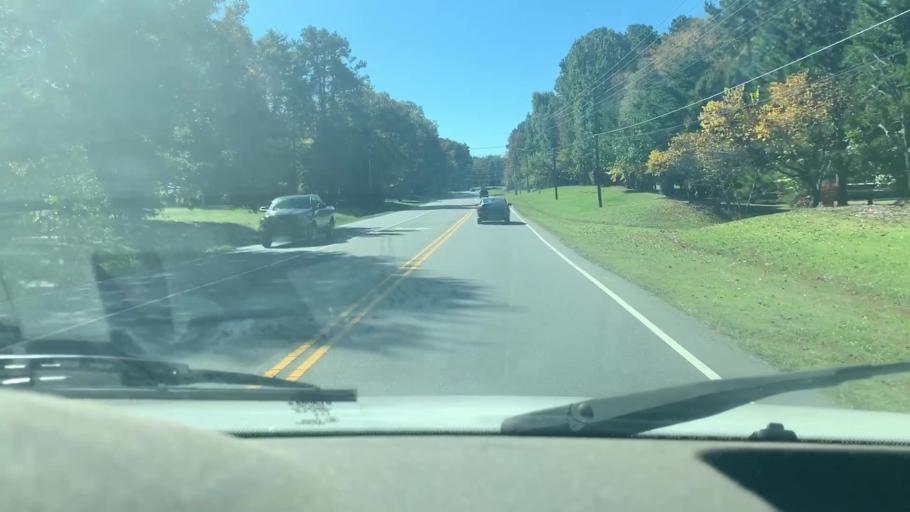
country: US
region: North Carolina
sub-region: Mecklenburg County
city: Huntersville
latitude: 35.4354
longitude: -80.9045
